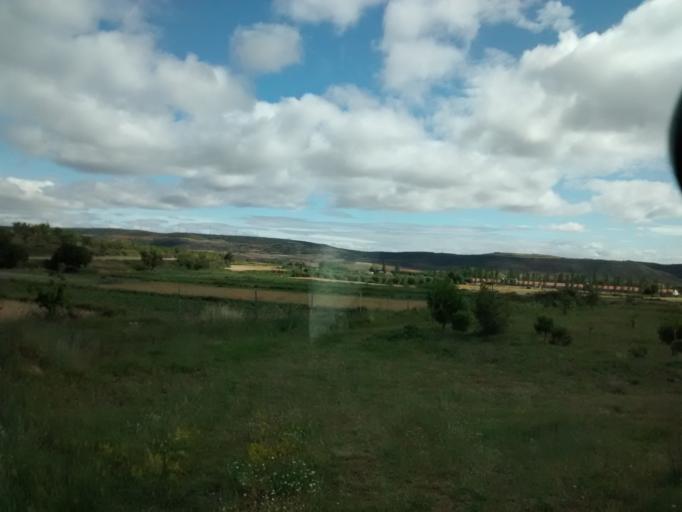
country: ES
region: Aragon
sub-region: Provincia de Zaragoza
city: Trasmoz
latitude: 41.8202
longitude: -1.7118
